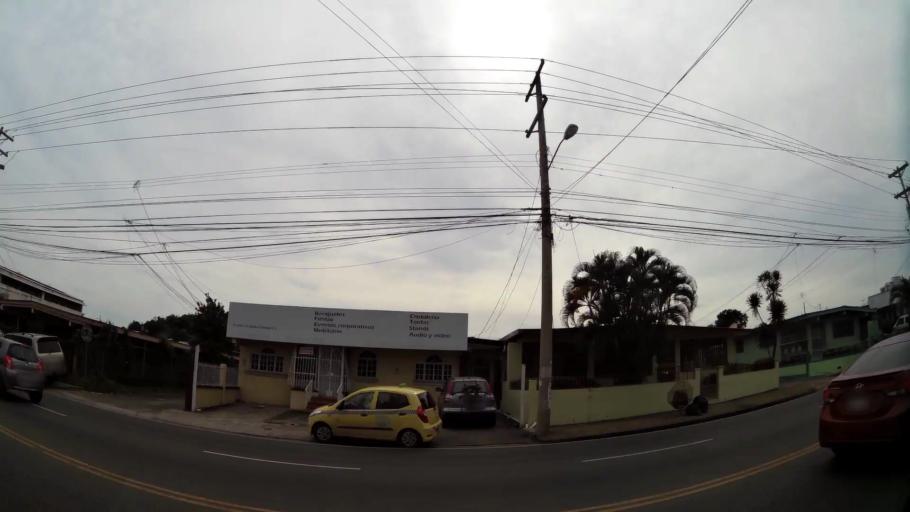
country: PA
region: Panama
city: Panama
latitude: 9.0205
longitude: -79.5238
